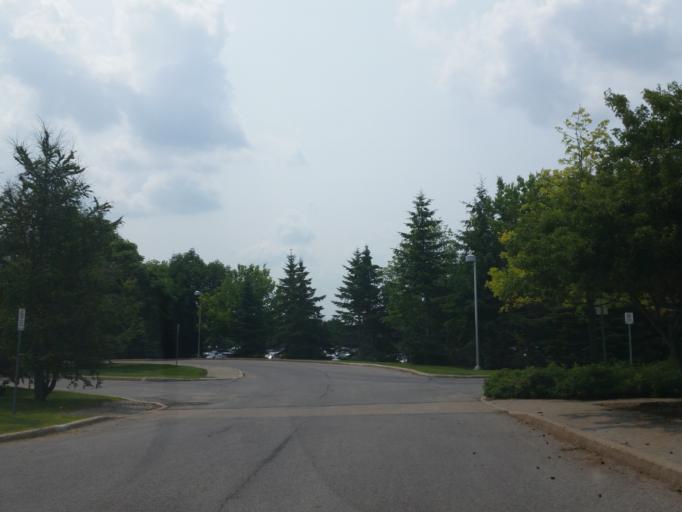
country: CA
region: Ontario
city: Bells Corners
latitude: 45.3446
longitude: -75.9109
